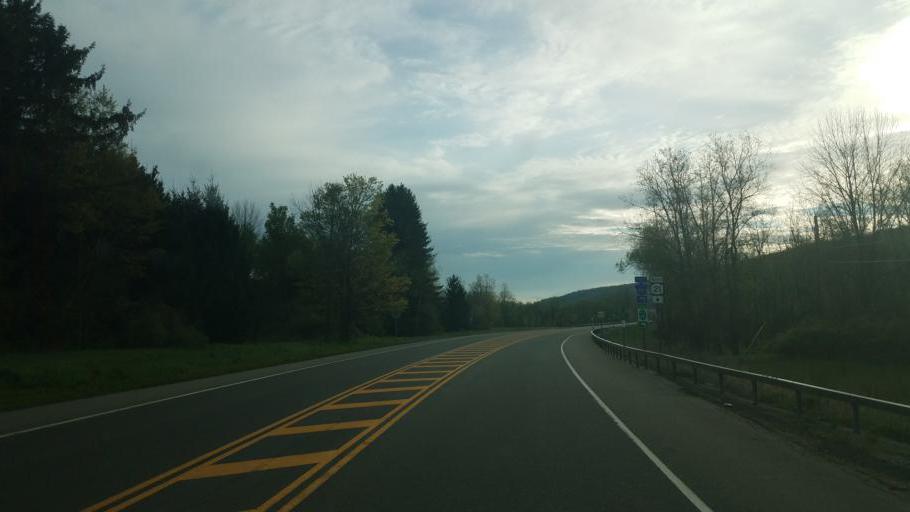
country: US
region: New York
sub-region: Steuben County
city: Hornell
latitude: 42.3373
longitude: -77.7239
